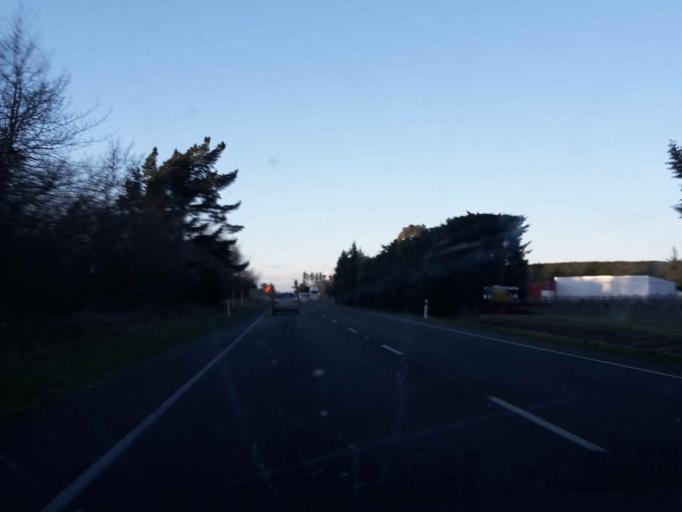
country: NZ
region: Canterbury
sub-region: Selwyn District
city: Burnham
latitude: -43.6170
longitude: 172.3101
